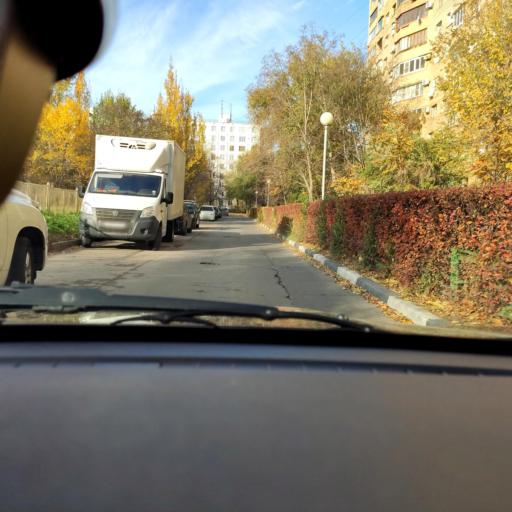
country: RU
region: Samara
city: Tol'yatti
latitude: 53.5148
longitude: 49.2700
